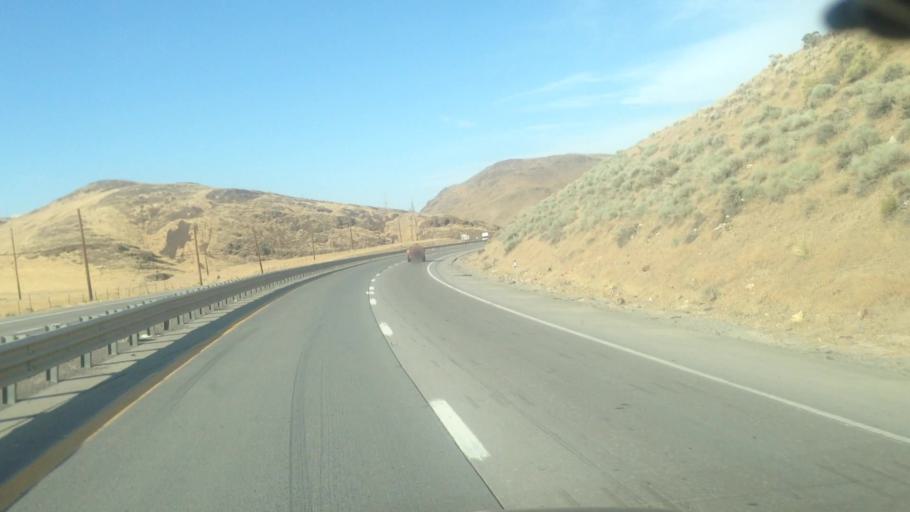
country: US
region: Nevada
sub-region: Washoe County
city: Sparks
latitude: 39.5290
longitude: -119.6159
